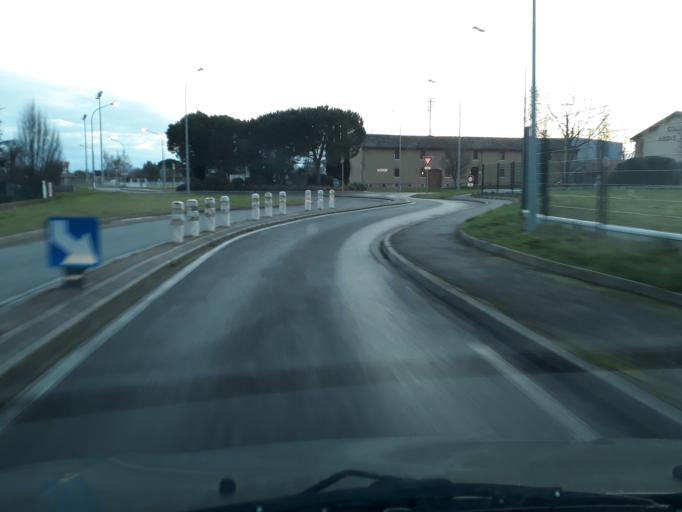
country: FR
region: Midi-Pyrenees
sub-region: Departement de la Haute-Garonne
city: Carbonne
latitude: 43.3101
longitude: 1.2303
